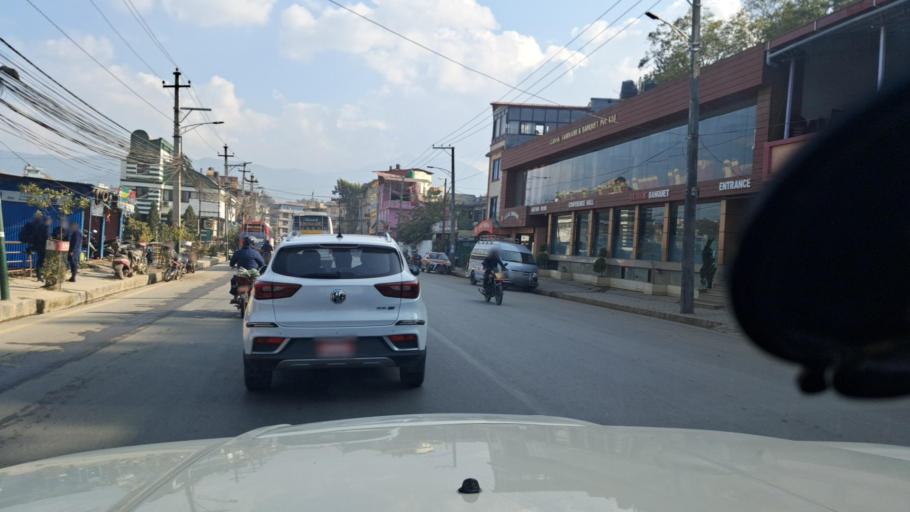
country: NP
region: Central Region
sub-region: Bagmati Zone
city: Patan
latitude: 27.6493
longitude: 85.3339
